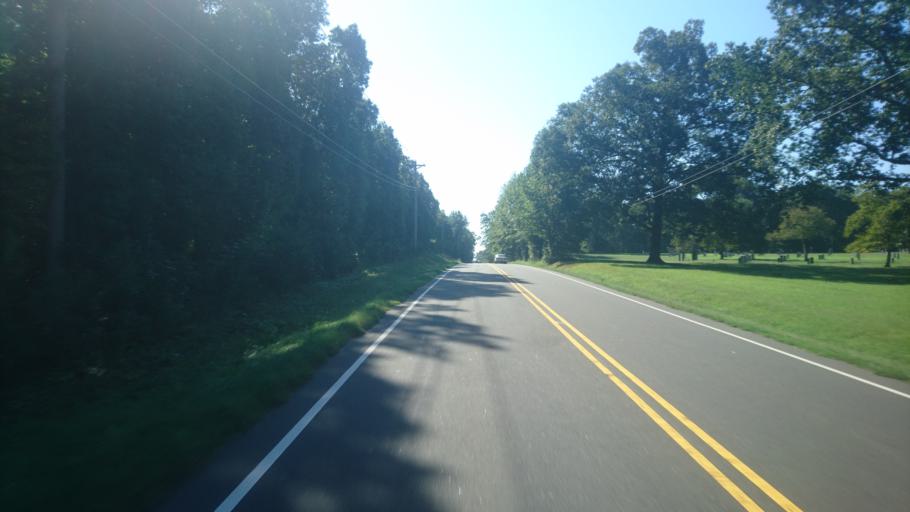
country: US
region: North Carolina
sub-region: Orange County
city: Hillsborough
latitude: 36.0134
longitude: -79.0713
